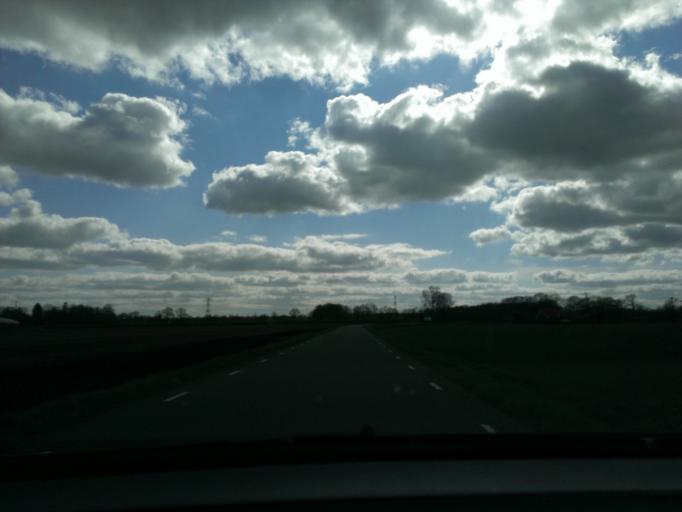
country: NL
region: Overijssel
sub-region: Gemeente Borne
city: Borne
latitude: 52.3170
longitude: 6.7134
